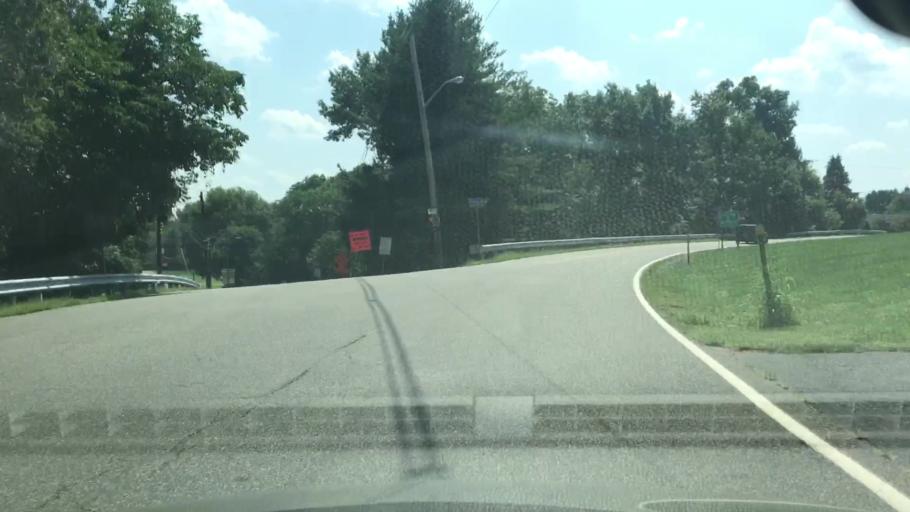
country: US
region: New Jersey
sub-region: Hunterdon County
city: Milford
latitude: 40.6067
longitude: -75.0771
